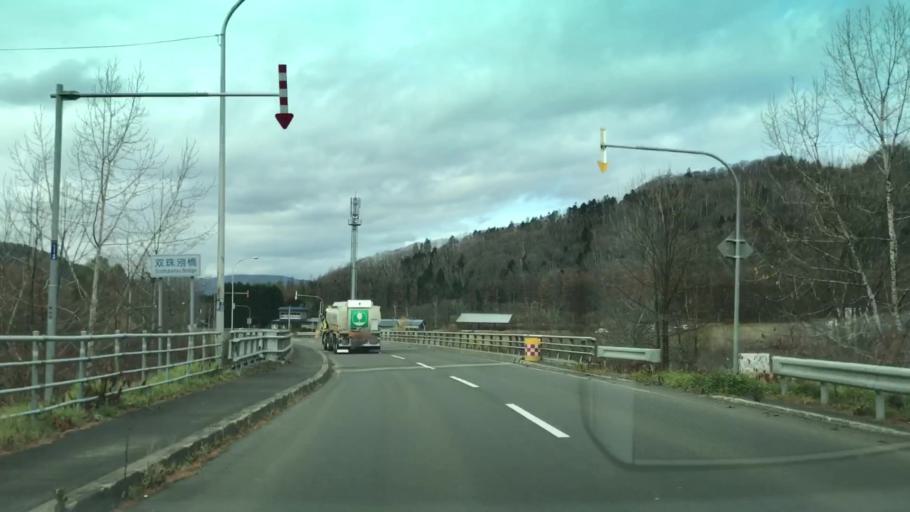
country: JP
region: Hokkaido
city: Shimo-furano
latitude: 42.9493
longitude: 142.4420
